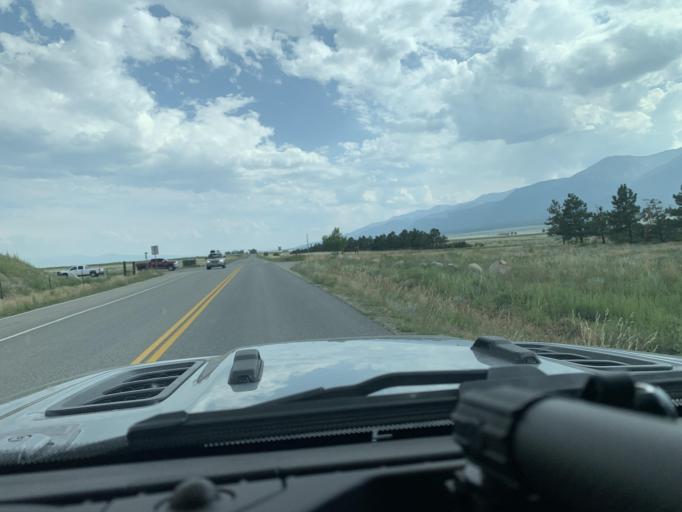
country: US
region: Colorado
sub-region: Chaffee County
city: Buena Vista
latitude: 38.8259
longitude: -106.1464
